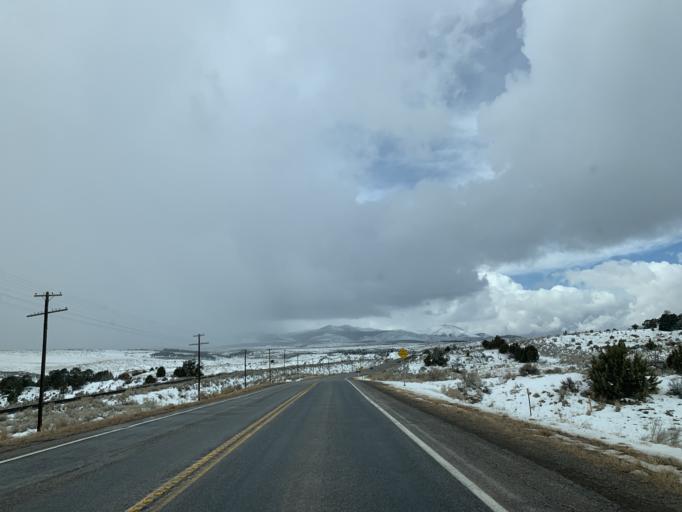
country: US
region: Utah
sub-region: Utah County
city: Genola
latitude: 39.9447
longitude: -112.2229
